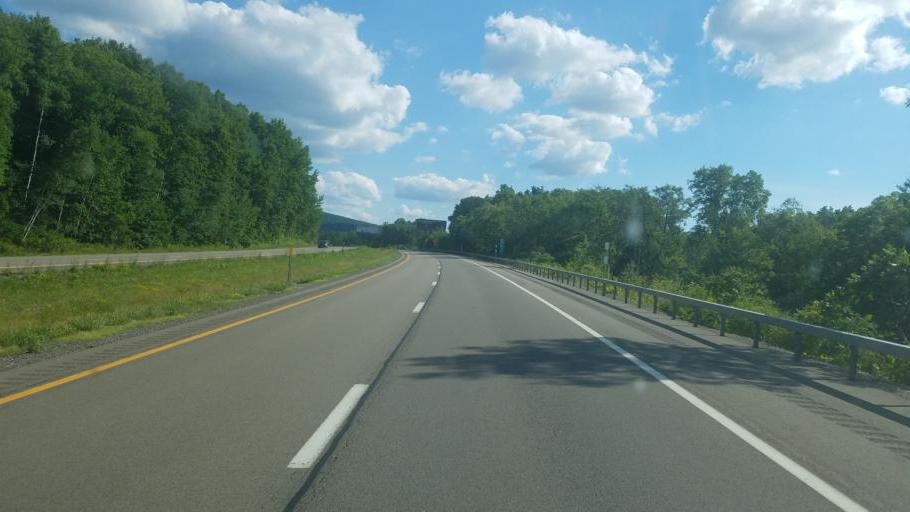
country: US
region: New York
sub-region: Cattaraugus County
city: Salamanca
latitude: 42.1350
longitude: -78.7783
